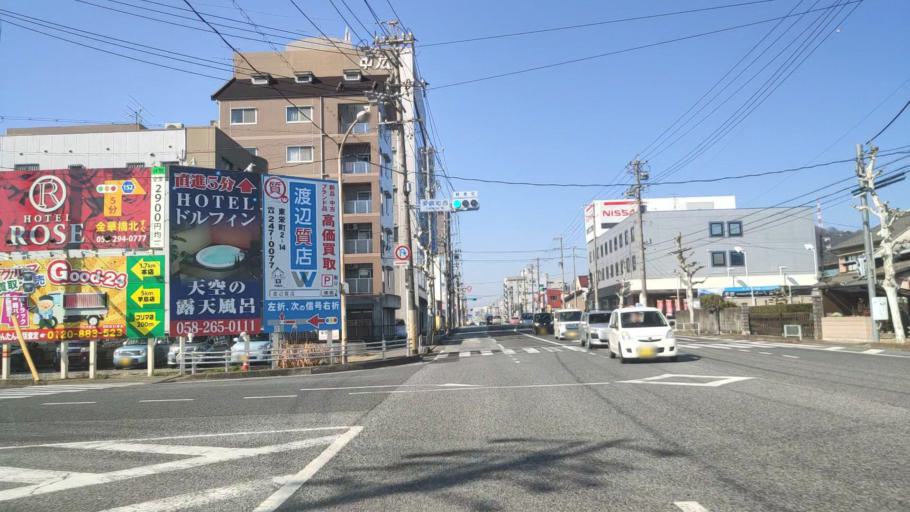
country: JP
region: Gifu
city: Gifu-shi
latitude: 35.4165
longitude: 136.7820
